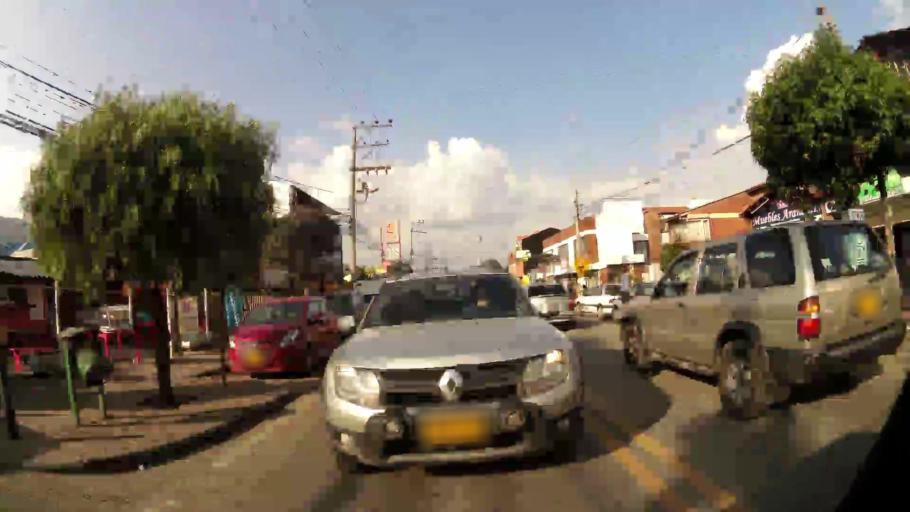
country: CO
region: Cundinamarca
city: Cota
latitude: 4.8084
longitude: -74.1030
